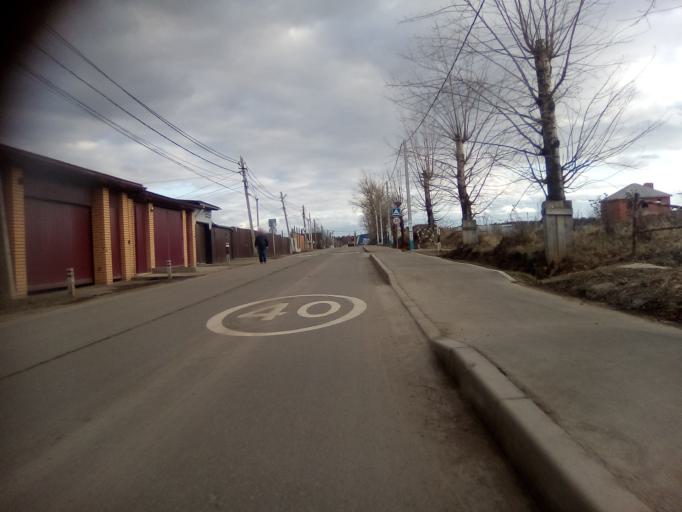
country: RU
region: Moskovskaya
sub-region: Leninskiy Rayon
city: Vnukovo
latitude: 55.5947
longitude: 37.3189
